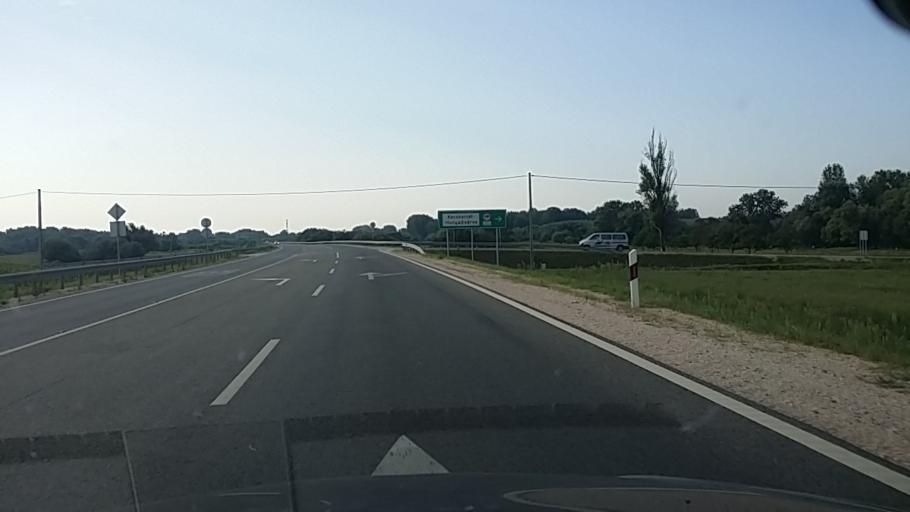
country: HU
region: Bacs-Kiskun
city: Kecskemet
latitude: 46.9191
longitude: 19.7265
